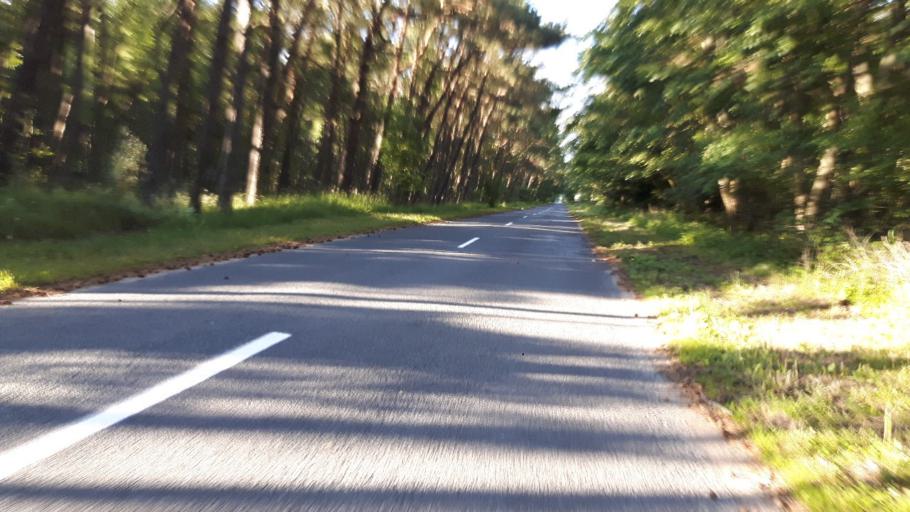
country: LT
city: Nida
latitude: 55.2576
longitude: 20.9357
